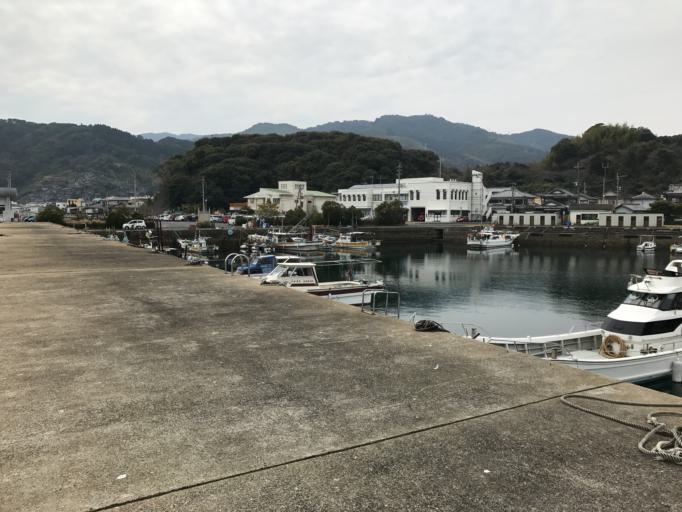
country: JP
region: Nagasaki
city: Nagasaki-shi
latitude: 32.7084
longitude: 129.9138
